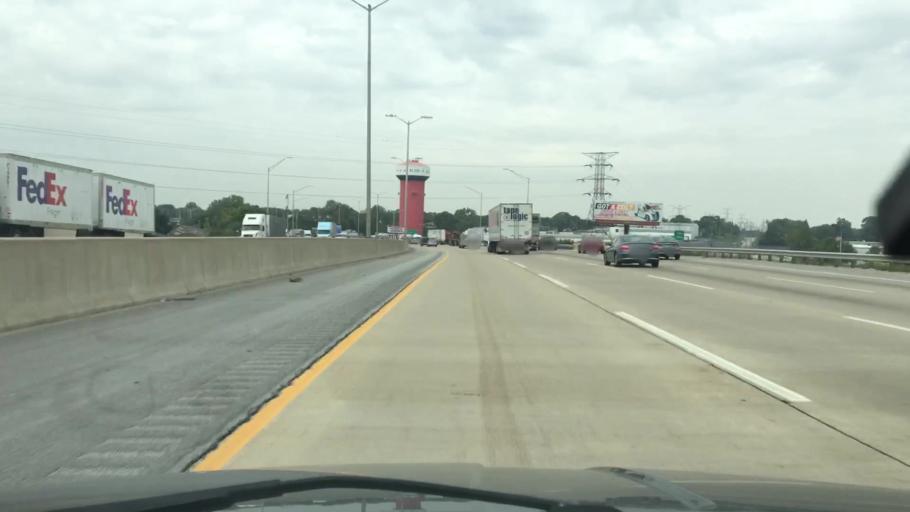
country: US
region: Illinois
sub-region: Cook County
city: Alsip
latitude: 41.6538
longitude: -87.7261
